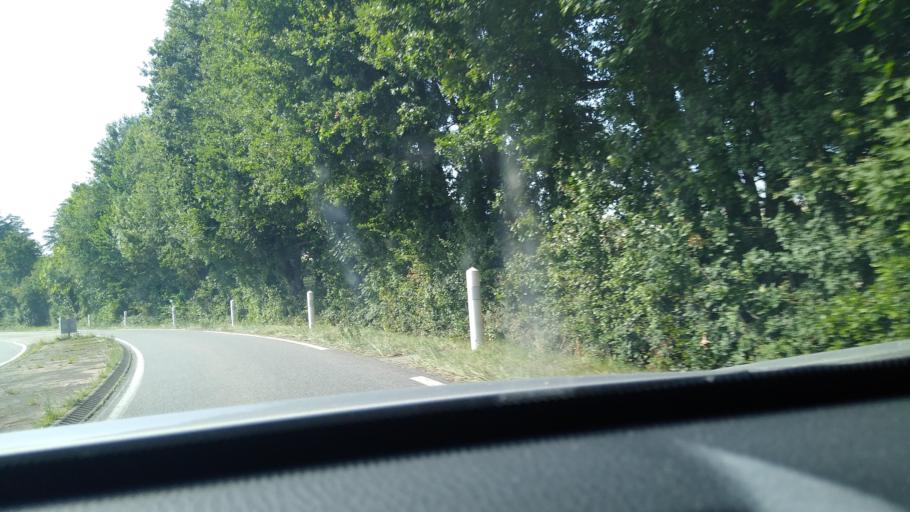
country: FR
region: Midi-Pyrenees
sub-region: Departement de la Haute-Garonne
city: Salies-du-Salat
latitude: 43.1169
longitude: 0.9363
